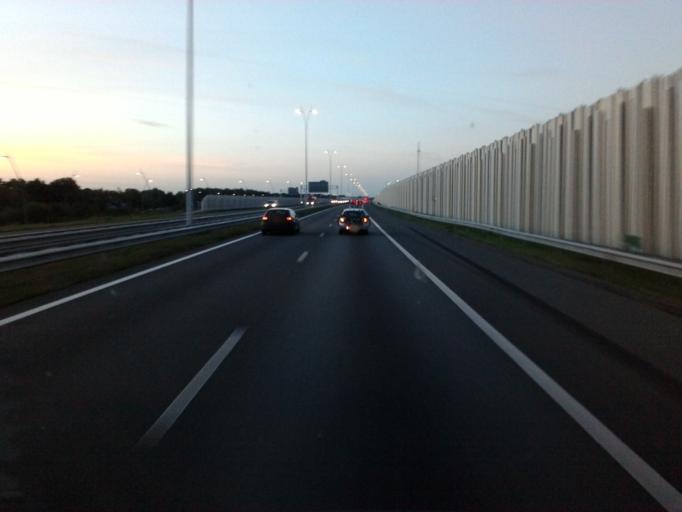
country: NL
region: North Brabant
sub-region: Gemeente Veldhoven
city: Veldhoven
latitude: 51.4135
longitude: 5.4298
